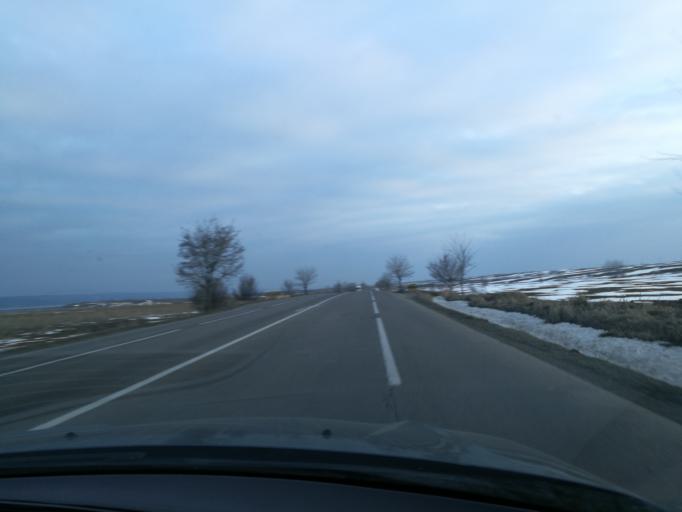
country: RO
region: Bacau
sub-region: Comuna Valea Seaca
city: Valea Seaca
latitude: 46.2604
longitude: 27.0729
